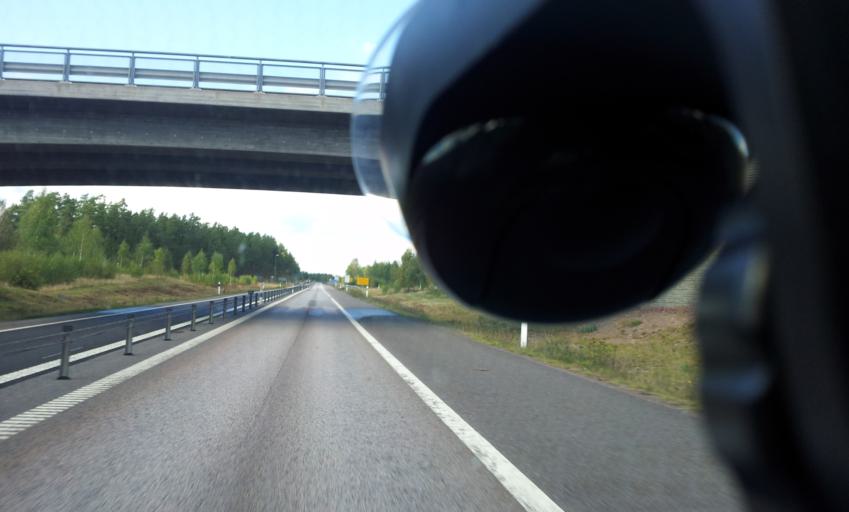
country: SE
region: Kalmar
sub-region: Oskarshamns Kommun
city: Oskarshamn
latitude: 57.3722
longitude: 16.4902
